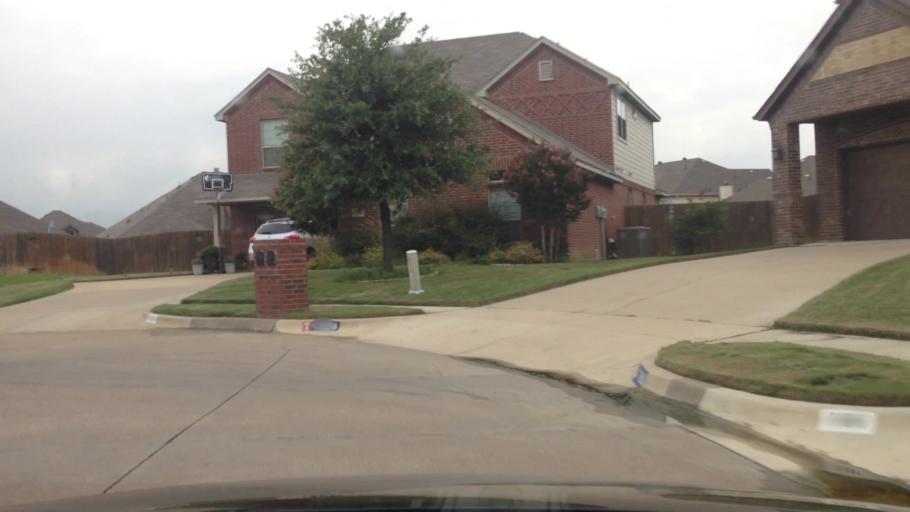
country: US
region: Texas
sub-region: Johnson County
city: Burleson
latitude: 32.5697
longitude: -97.3335
